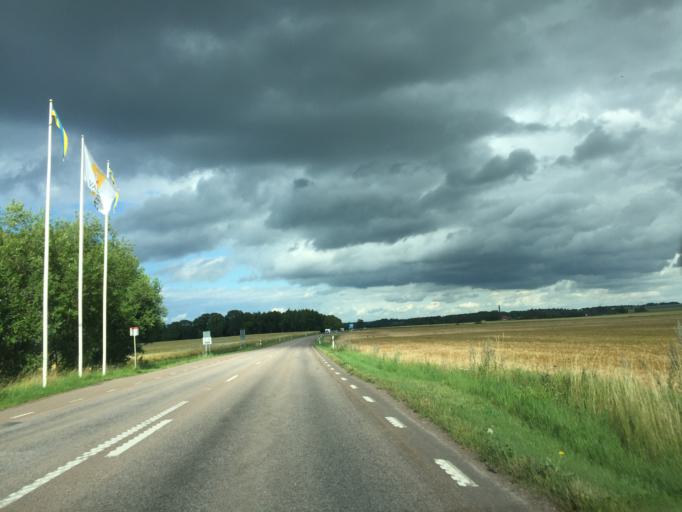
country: SE
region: OEstergoetland
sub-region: Vadstena Kommun
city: Vadstena
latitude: 58.4540
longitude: 14.9123
